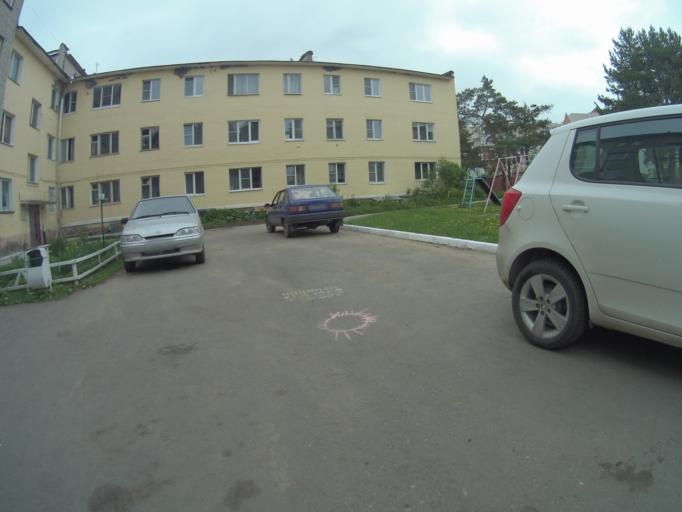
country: RU
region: Vladimir
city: Kommunar
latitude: 56.1077
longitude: 40.4335
